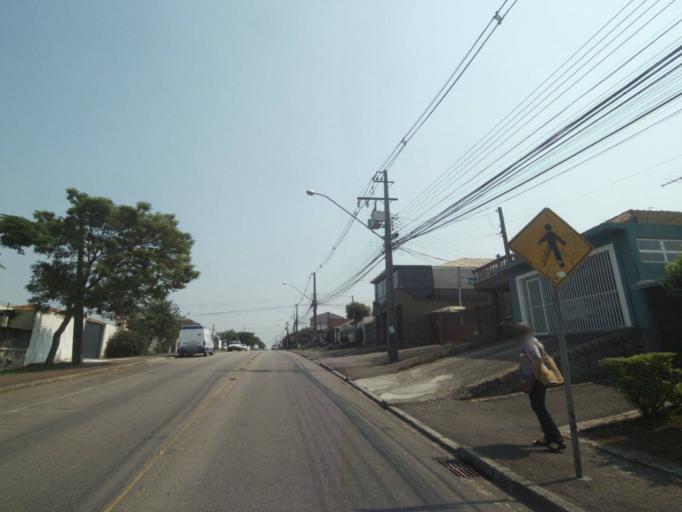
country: BR
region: Parana
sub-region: Sao Jose Dos Pinhais
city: Sao Jose dos Pinhais
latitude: -25.5228
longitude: -49.2470
